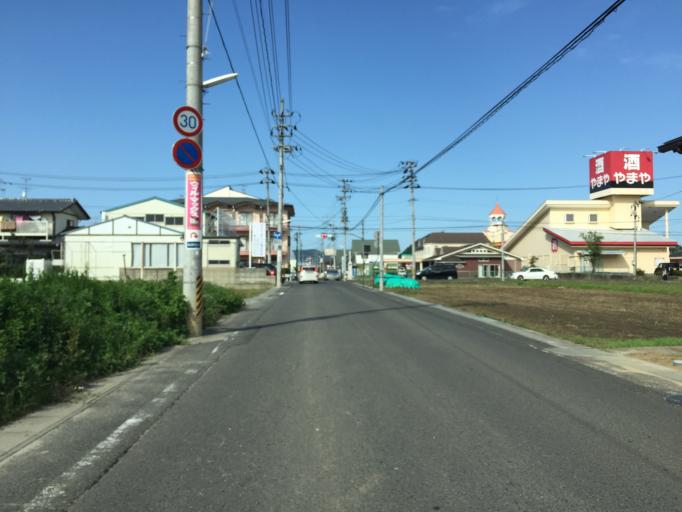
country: JP
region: Fukushima
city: Fukushima-shi
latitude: 37.7325
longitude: 140.4652
